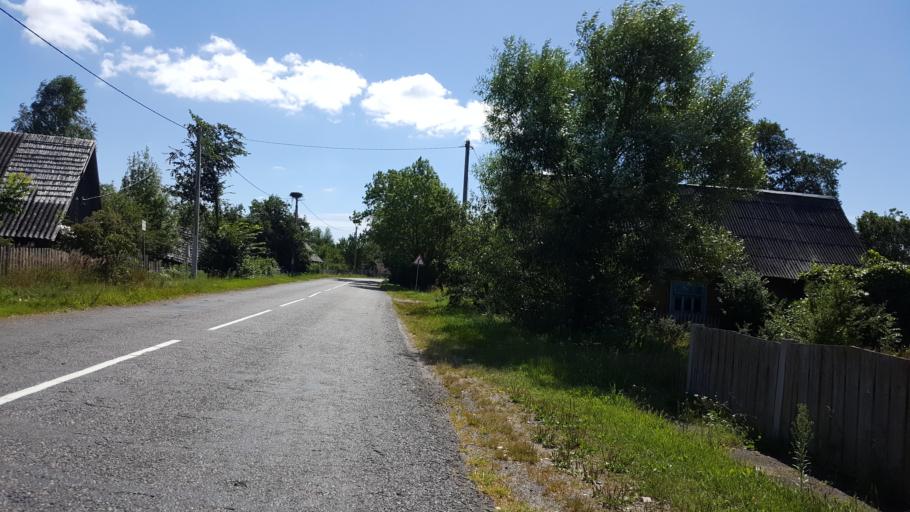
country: BY
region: Brest
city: Zhabinka
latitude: 52.3641
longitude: 24.1498
